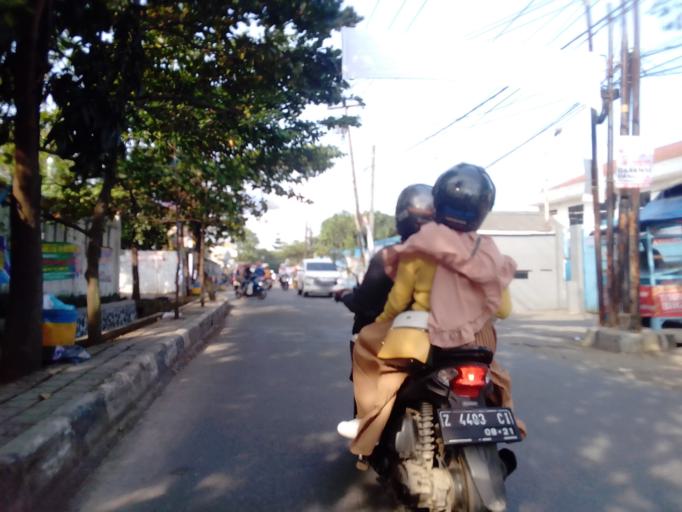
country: ID
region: West Java
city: Cileunyi
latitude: -6.9239
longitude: 107.6993
